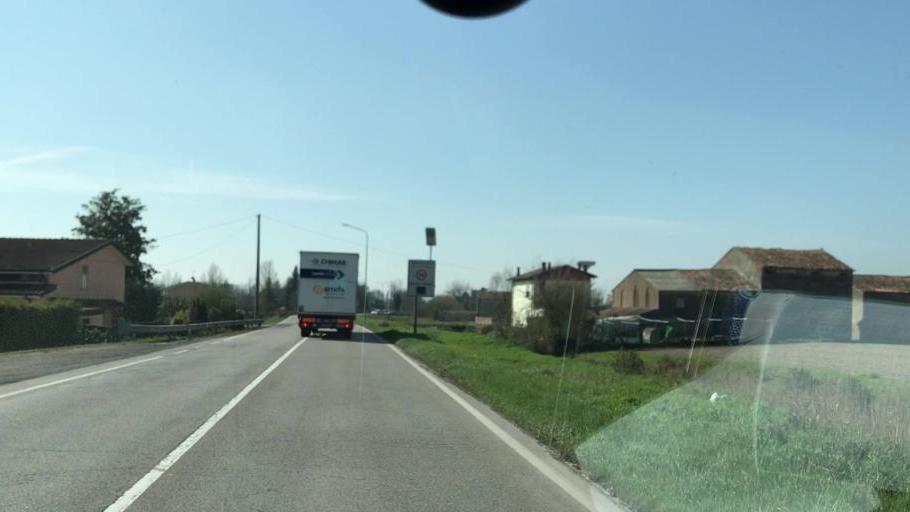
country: IT
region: Veneto
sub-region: Provincia di Rovigo
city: Castelnovo Bariano
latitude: 45.0308
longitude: 11.2986
